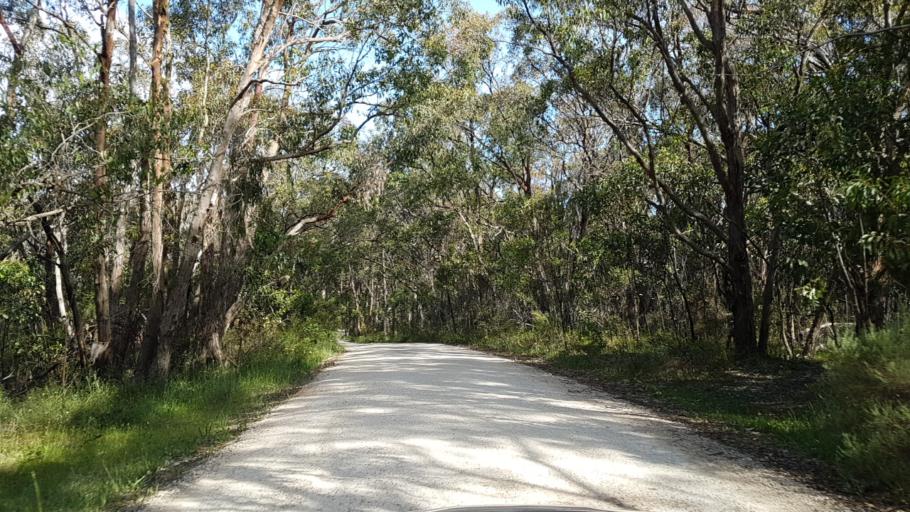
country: AU
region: South Australia
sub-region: Adelaide Hills
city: Adelaide Hills
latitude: -34.9095
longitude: 138.7498
